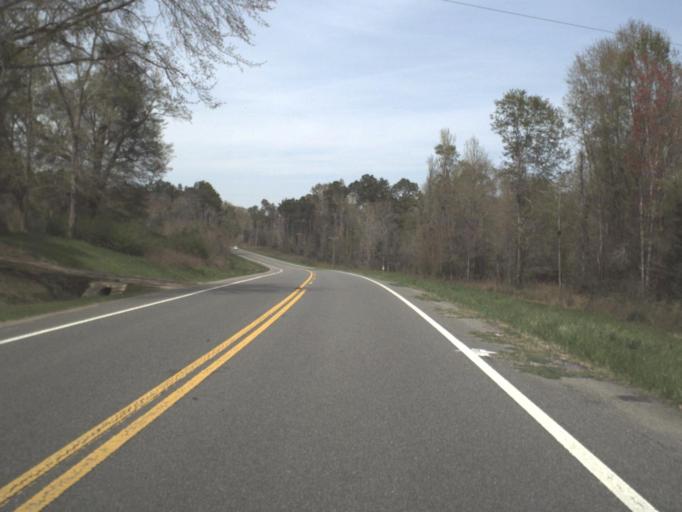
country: US
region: Alabama
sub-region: Geneva County
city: Geneva
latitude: 30.9352
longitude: -85.9676
